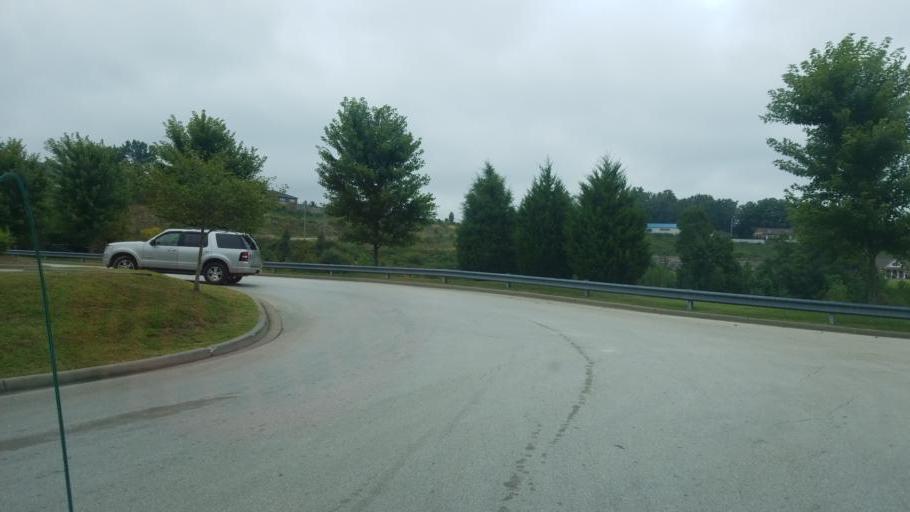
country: US
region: Kentucky
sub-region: Rowan County
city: Morehead
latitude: 38.2002
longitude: -83.4796
